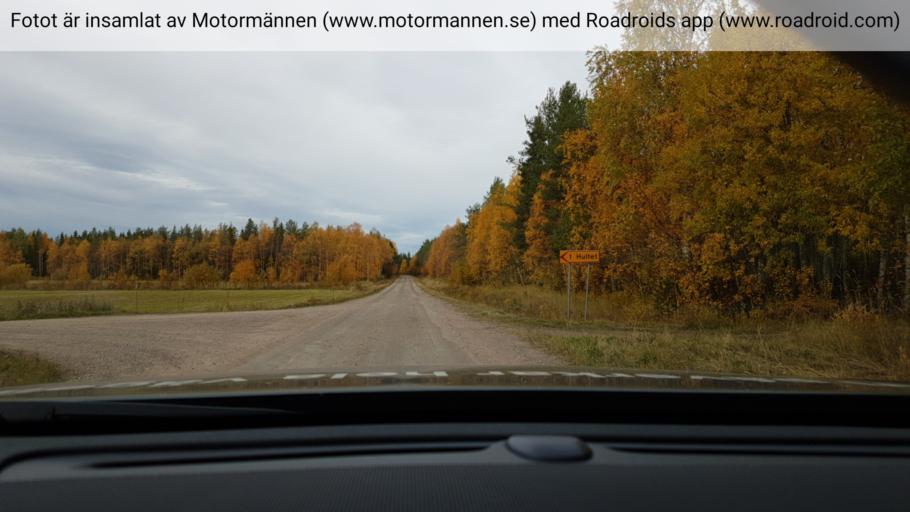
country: SE
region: Norrbotten
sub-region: Overkalix Kommun
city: OEverkalix
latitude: 66.2963
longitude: 22.9412
